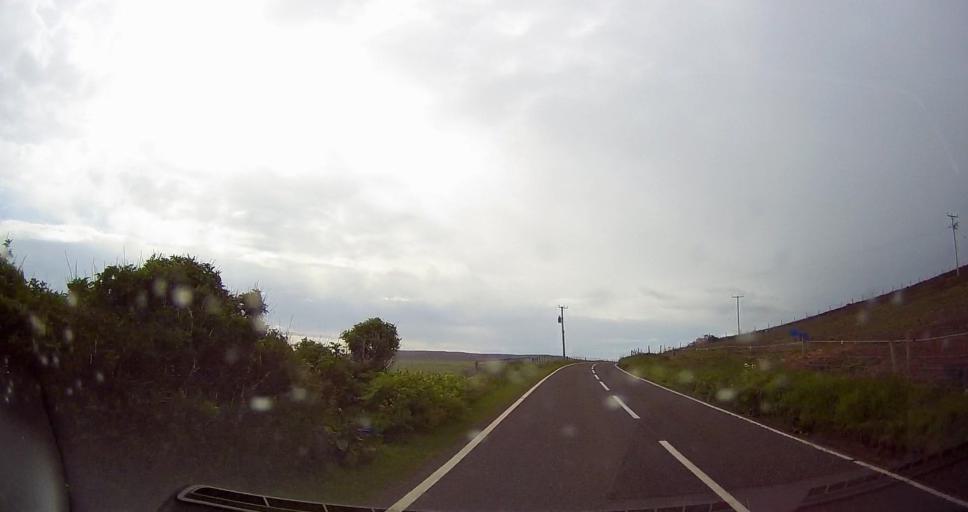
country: GB
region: Scotland
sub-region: Orkney Islands
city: Stromness
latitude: 59.1093
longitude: -3.2850
